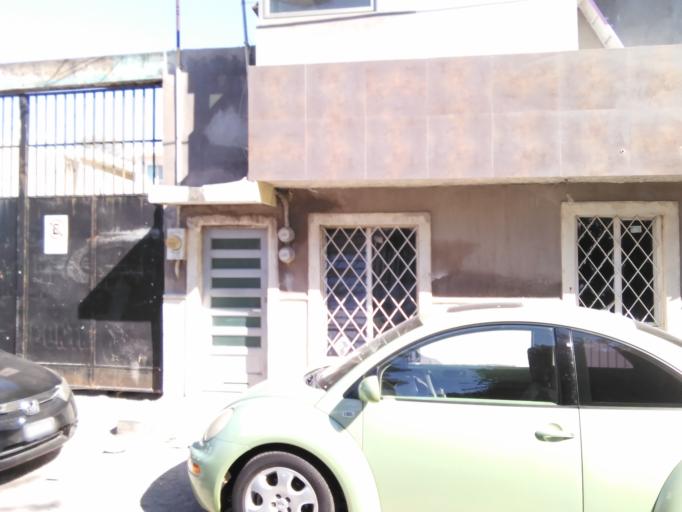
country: MX
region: Nayarit
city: Tepic
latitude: 21.4839
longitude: -104.8896
